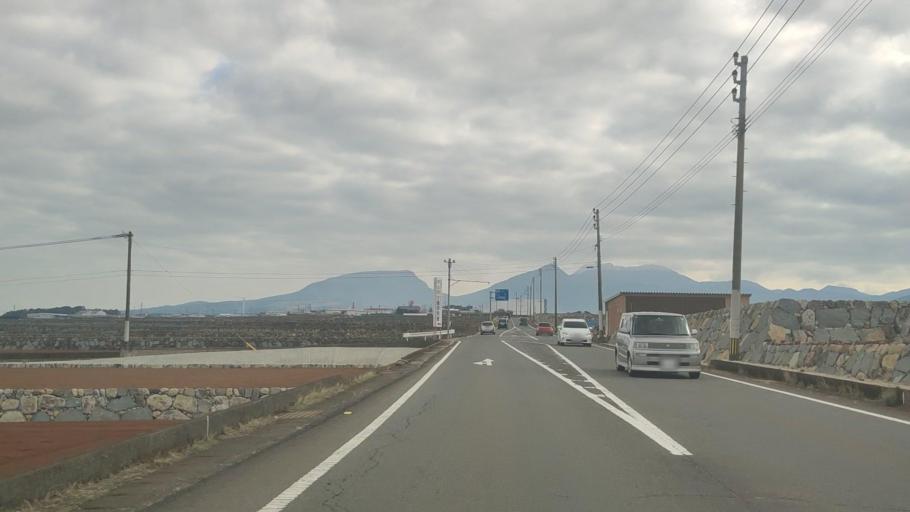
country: JP
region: Nagasaki
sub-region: Isahaya-shi
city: Isahaya
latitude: 32.7969
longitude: 130.1548
